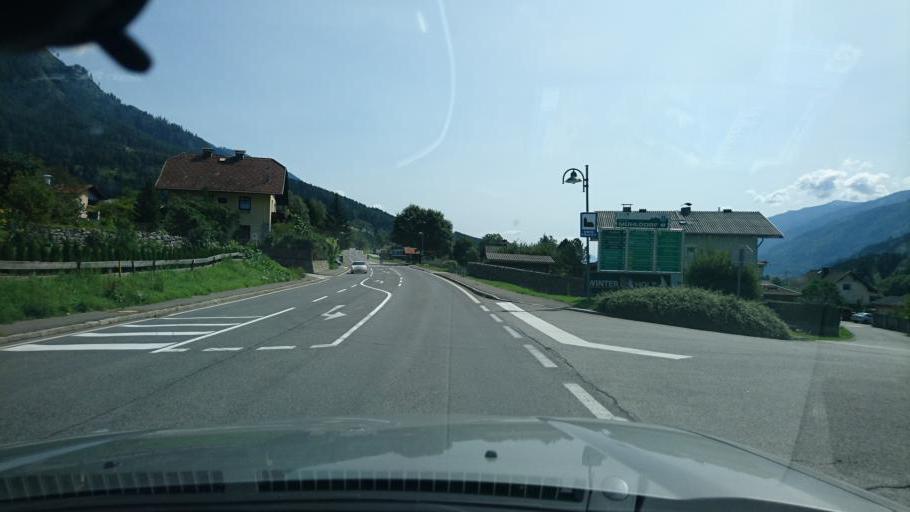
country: AT
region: Carinthia
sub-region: Politischer Bezirk Spittal an der Drau
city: Muhldorf
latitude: 46.8586
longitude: 13.3408
